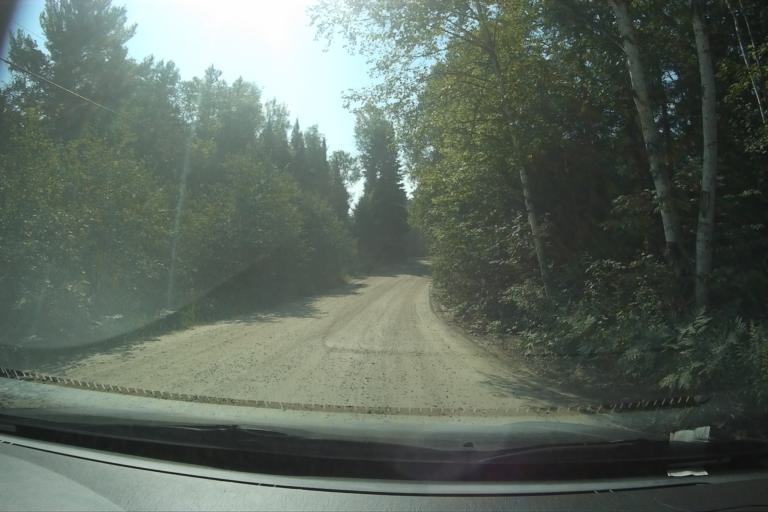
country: CA
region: Ontario
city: Huntsville
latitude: 45.5654
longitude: -78.7060
